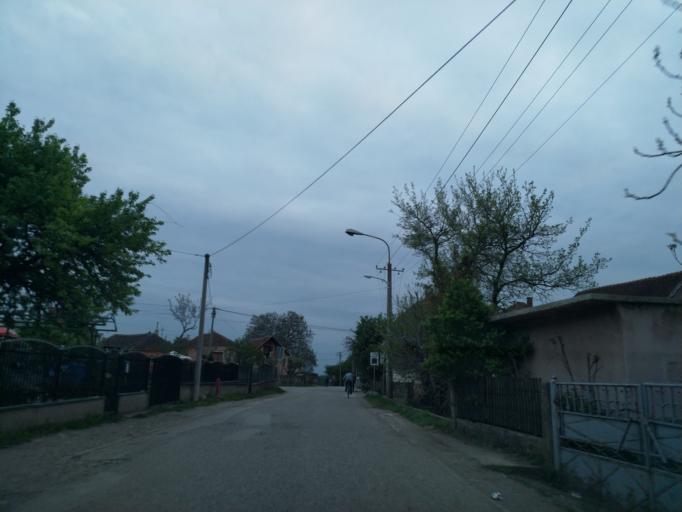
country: RS
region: Central Serbia
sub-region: Pomoravski Okrug
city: Paracin
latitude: 43.9403
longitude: 21.4944
